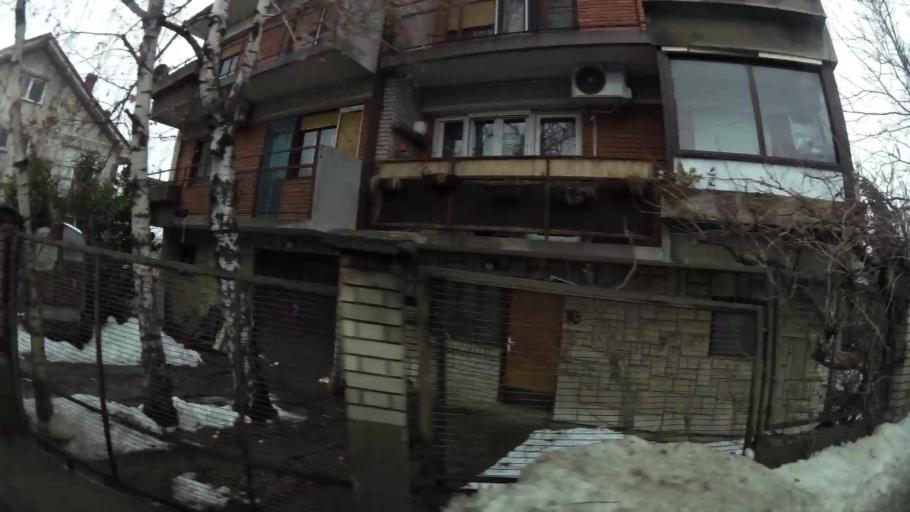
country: RS
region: Central Serbia
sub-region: Belgrade
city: Zvezdara
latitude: 44.7724
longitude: 20.5355
